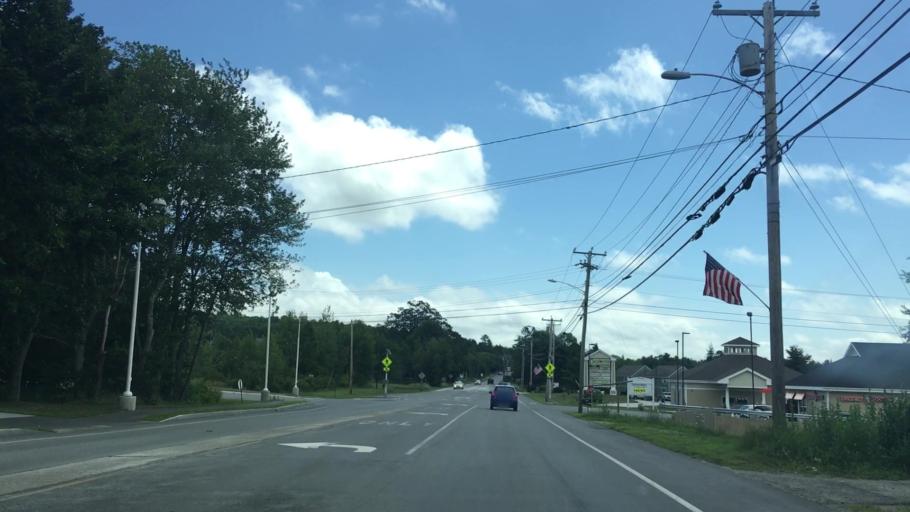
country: US
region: Maine
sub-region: Penobscot County
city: Hermon
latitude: 44.8065
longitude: -68.9037
